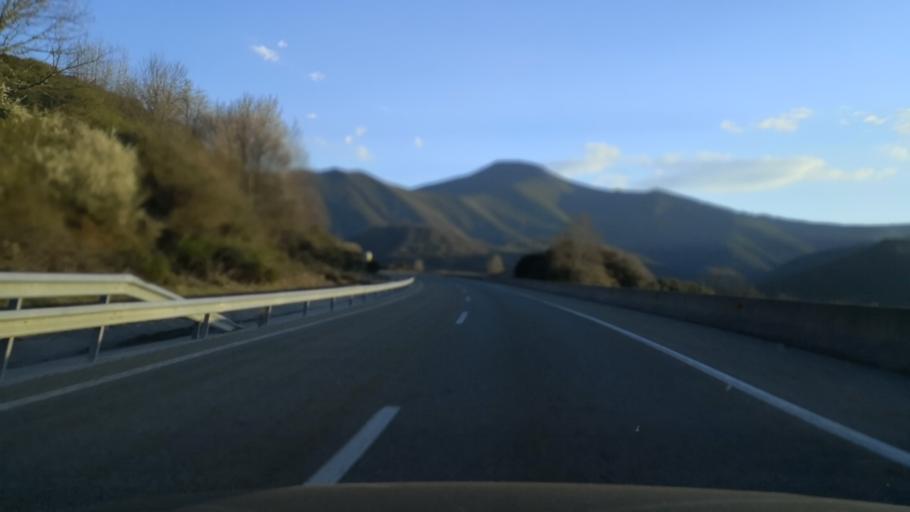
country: ES
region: Castille and Leon
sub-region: Provincia de Leon
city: Vega de Valcarce
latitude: 42.6805
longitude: -6.9891
